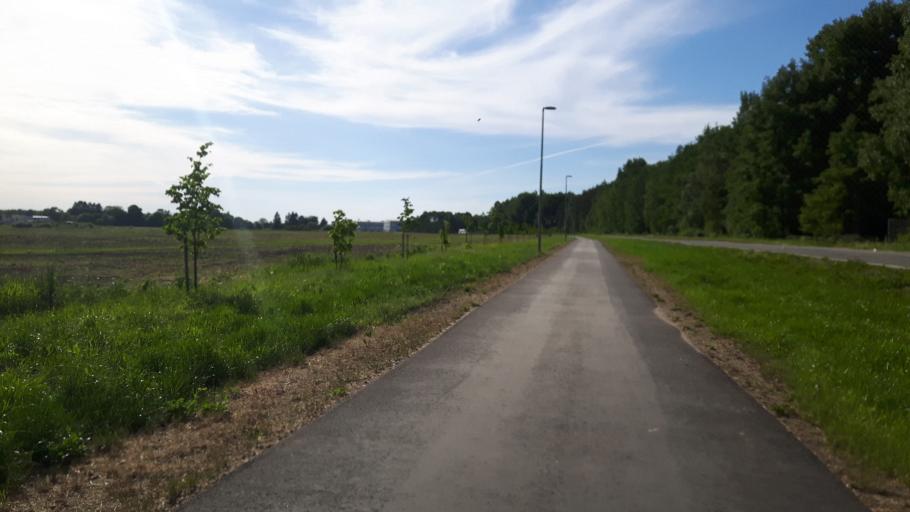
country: EE
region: Harju
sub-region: Joelaehtme vald
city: Loo
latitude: 59.4290
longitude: 24.9824
